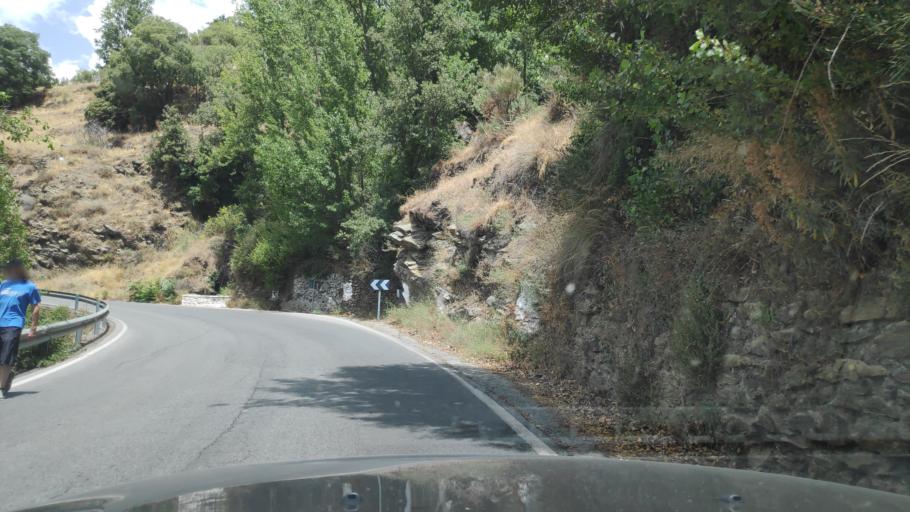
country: ES
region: Andalusia
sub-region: Provincia de Granada
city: Bubion
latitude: 36.9549
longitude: -3.3552
